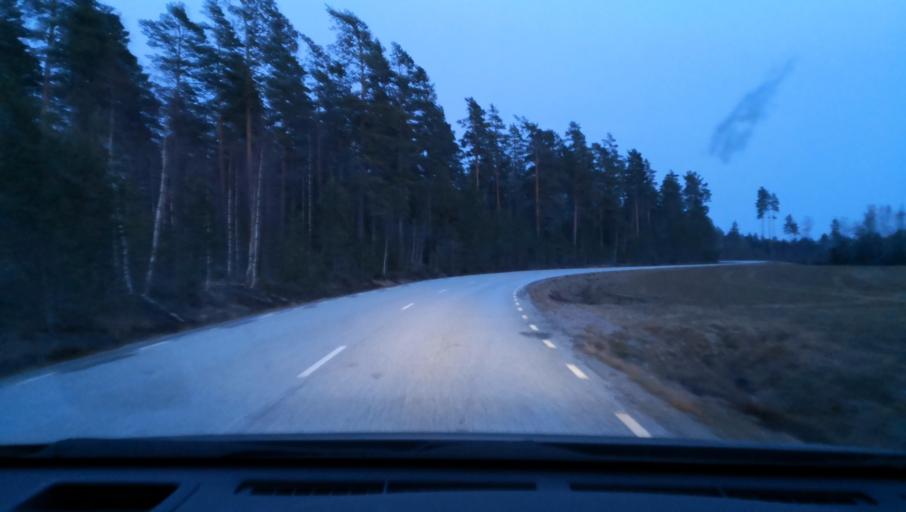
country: SE
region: OErebro
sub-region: Lindesbergs Kommun
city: Frovi
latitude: 59.5882
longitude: 15.4371
